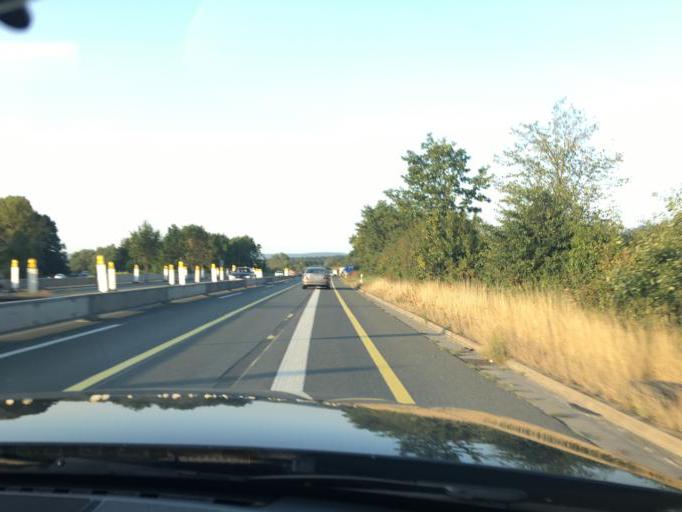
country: DE
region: Bavaria
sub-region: Upper Franconia
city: Forchheim
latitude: 49.7420
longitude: 11.0560
